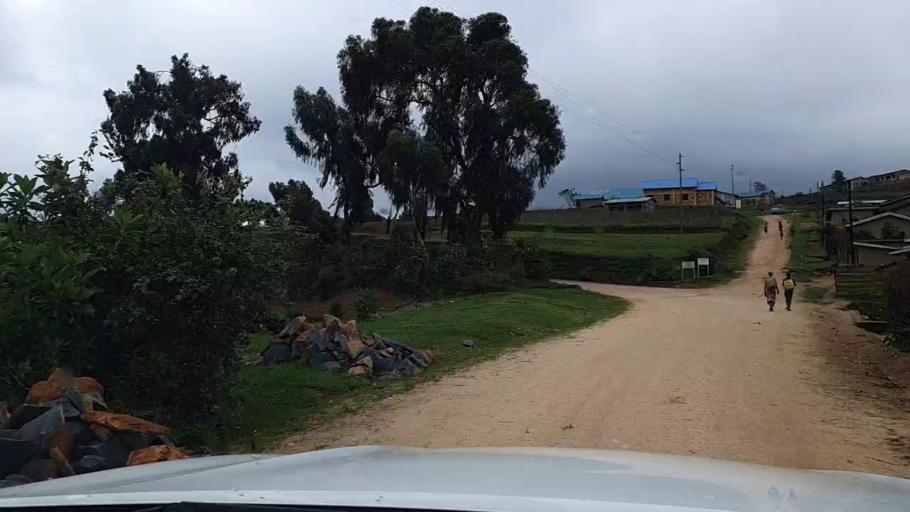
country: RW
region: Southern Province
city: Nzega
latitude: -2.3764
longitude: 29.3818
